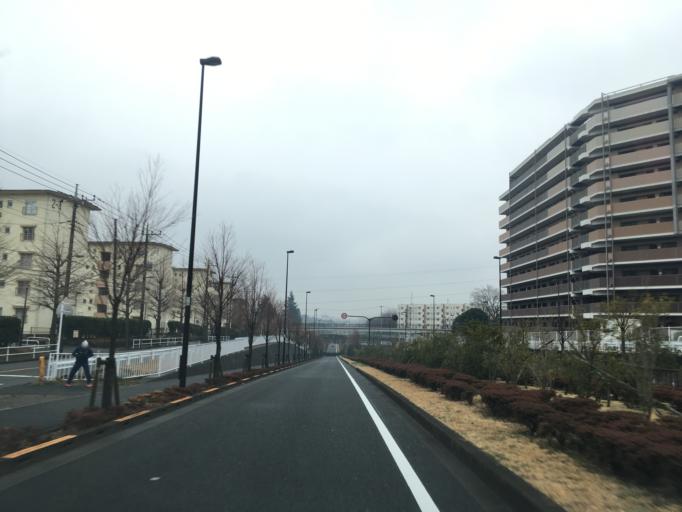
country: JP
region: Tokyo
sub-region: Machida-shi
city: Machida
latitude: 35.5697
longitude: 139.4295
